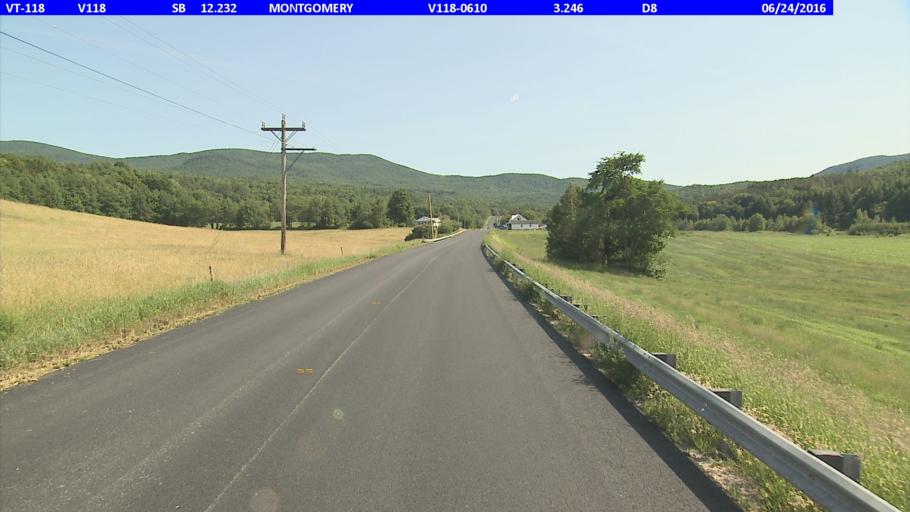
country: US
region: Vermont
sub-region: Franklin County
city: Richford
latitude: 44.8445
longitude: -72.6100
